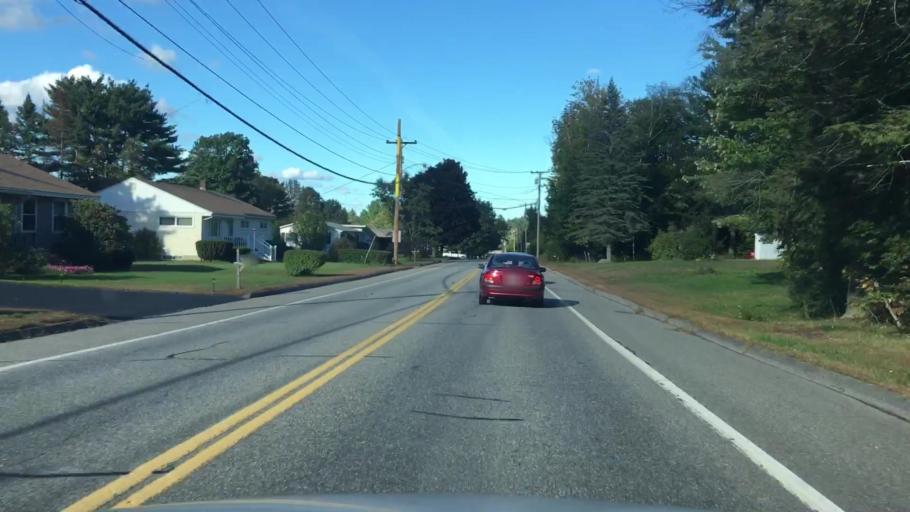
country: US
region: Maine
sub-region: Androscoggin County
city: Lewiston
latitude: 44.0915
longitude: -70.1621
